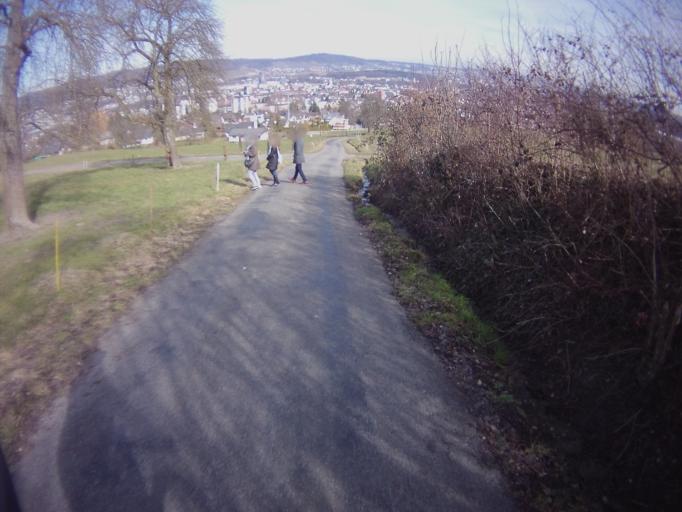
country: CH
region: Zurich
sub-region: Bezirk Dietikon
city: Dietikon / Almend
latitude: 47.3983
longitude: 8.3811
